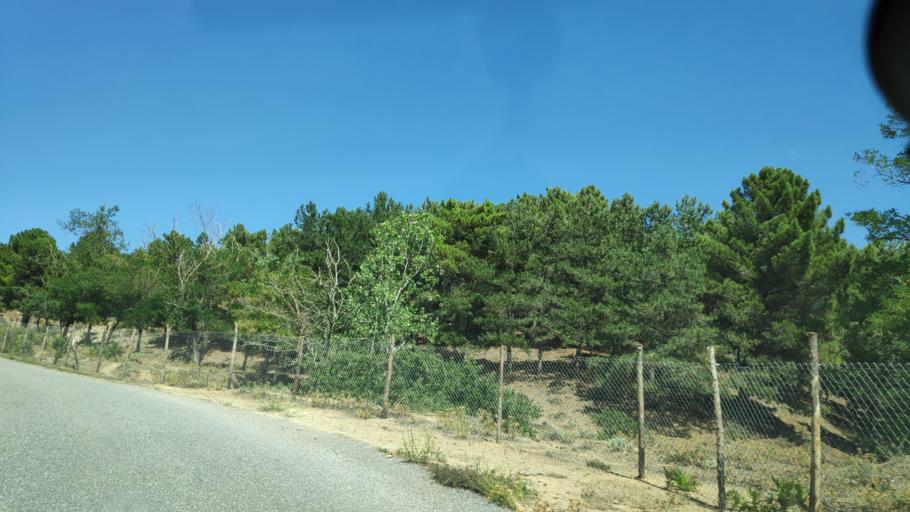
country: IT
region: Calabria
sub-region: Provincia di Reggio Calabria
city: Bova
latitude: 38.0205
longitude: 15.9353
